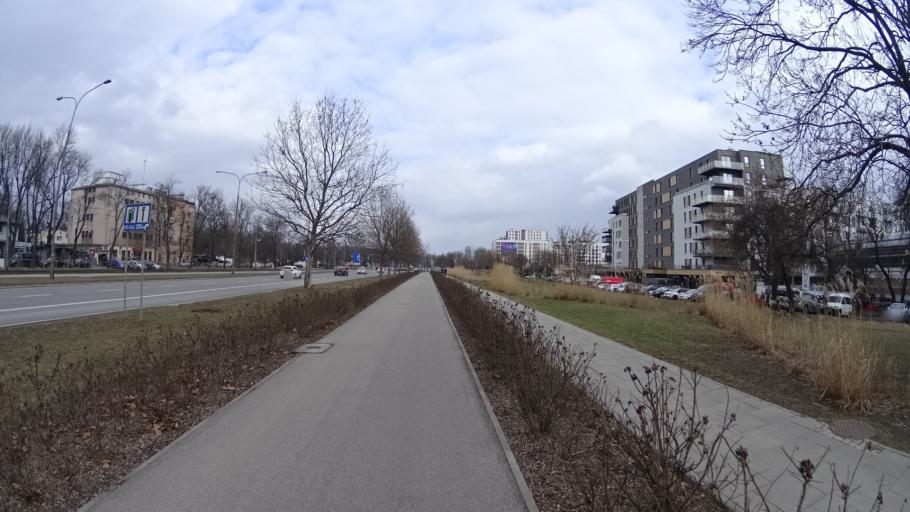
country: PL
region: Masovian Voivodeship
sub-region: Warszawa
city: Bemowo
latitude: 52.2248
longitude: 20.9335
